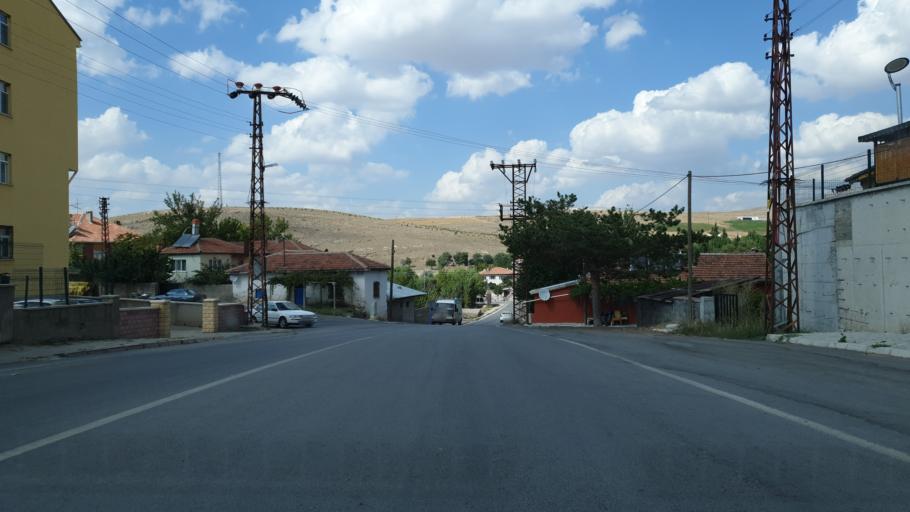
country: TR
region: Kayseri
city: Felahiye
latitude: 39.0911
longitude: 35.5695
